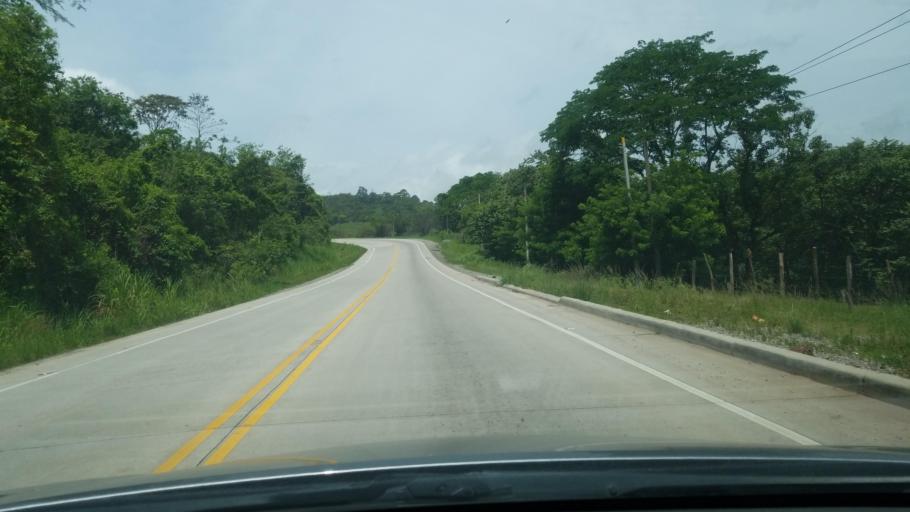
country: HN
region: Copan
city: Agua Caliente
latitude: 14.8636
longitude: -88.7882
